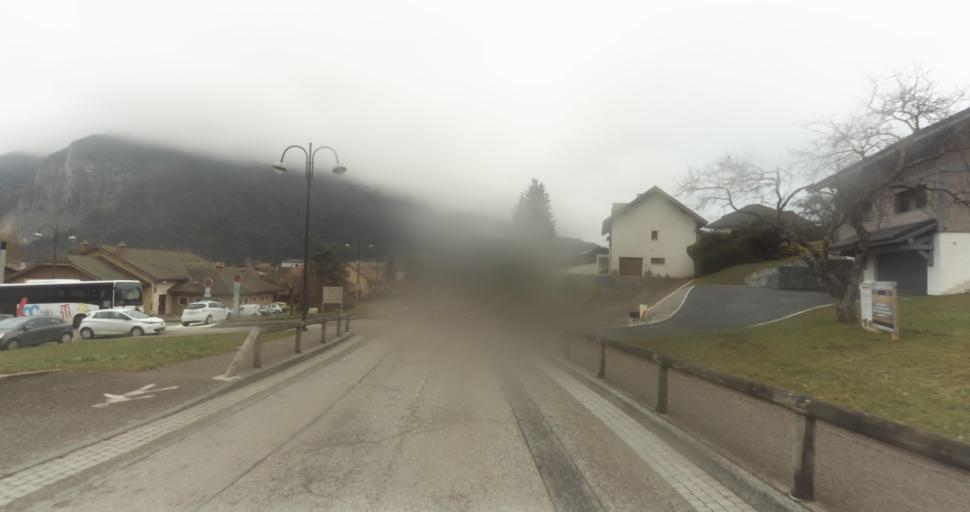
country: FR
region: Rhone-Alpes
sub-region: Departement de la Haute-Savoie
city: Thorens-Glieres
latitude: 45.9990
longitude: 6.2505
